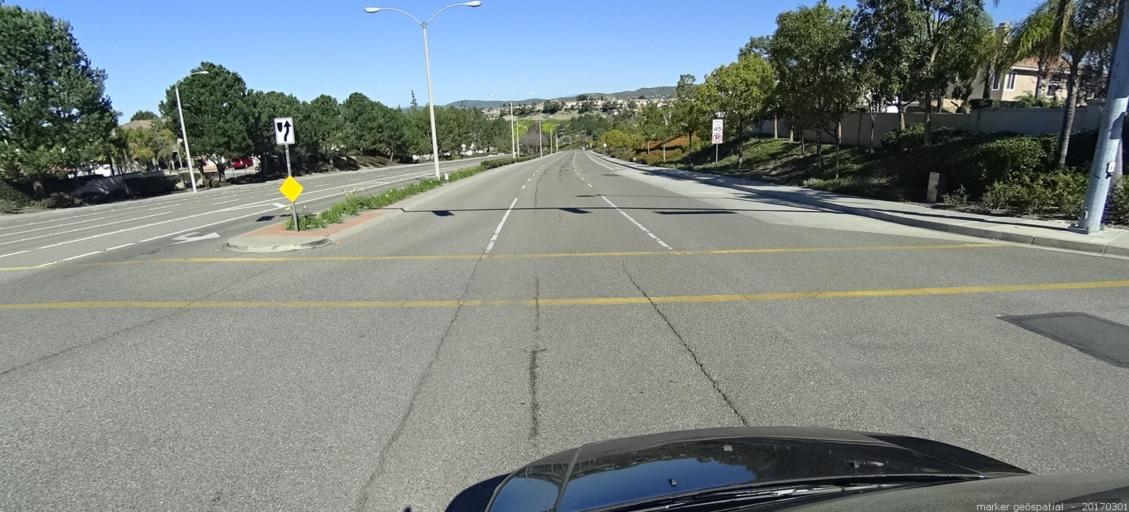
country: US
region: California
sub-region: Orange County
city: Yorba Linda
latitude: 33.8565
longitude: -117.7263
